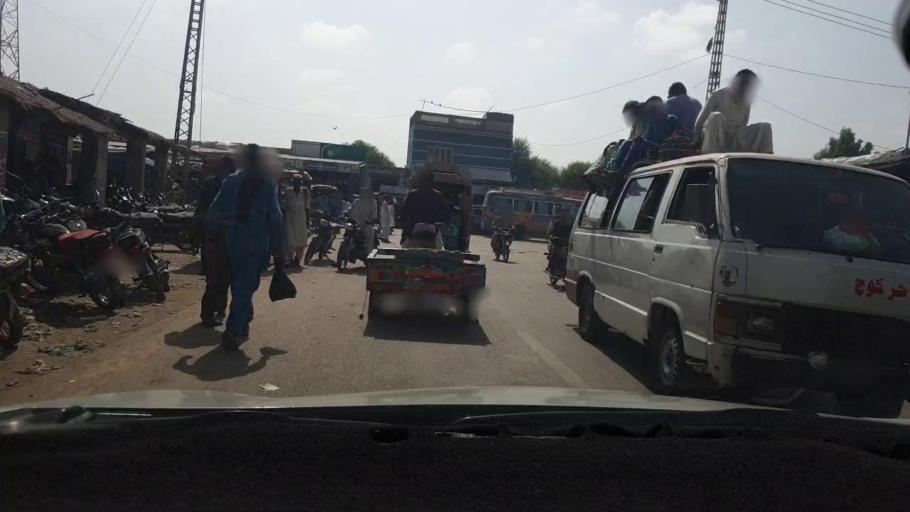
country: PK
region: Sindh
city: Mirpur Khas
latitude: 25.7090
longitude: 69.1281
